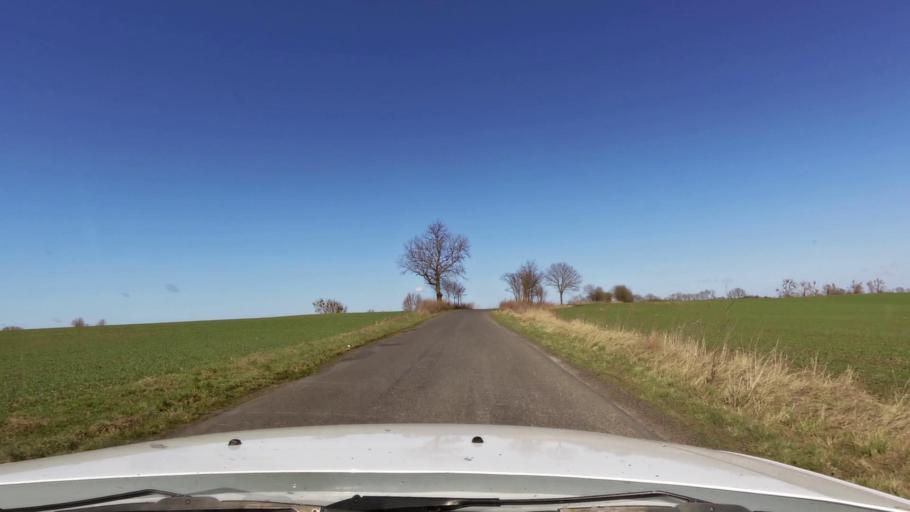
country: PL
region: West Pomeranian Voivodeship
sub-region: Powiat gryfinski
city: Cedynia
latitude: 52.8721
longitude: 14.2872
